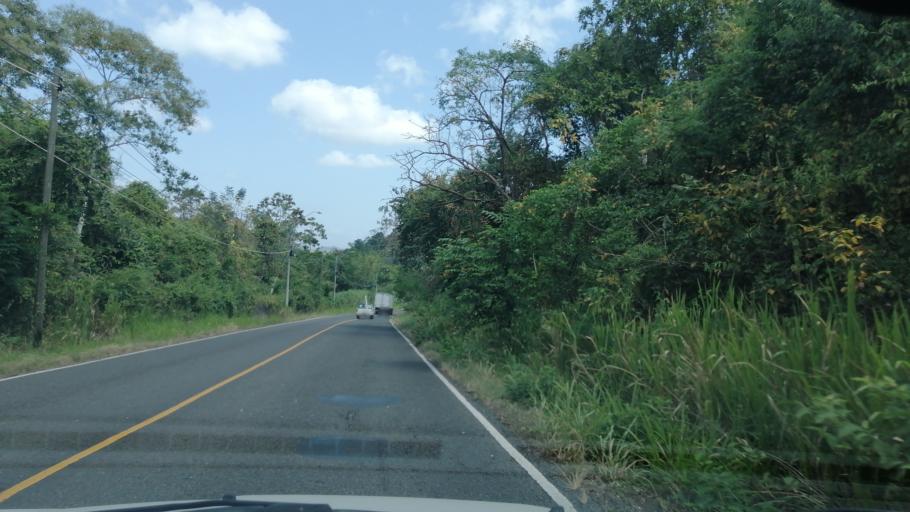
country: PA
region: Panama
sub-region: Distrito de Panama
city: Ancon
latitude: 8.9116
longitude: -79.5682
